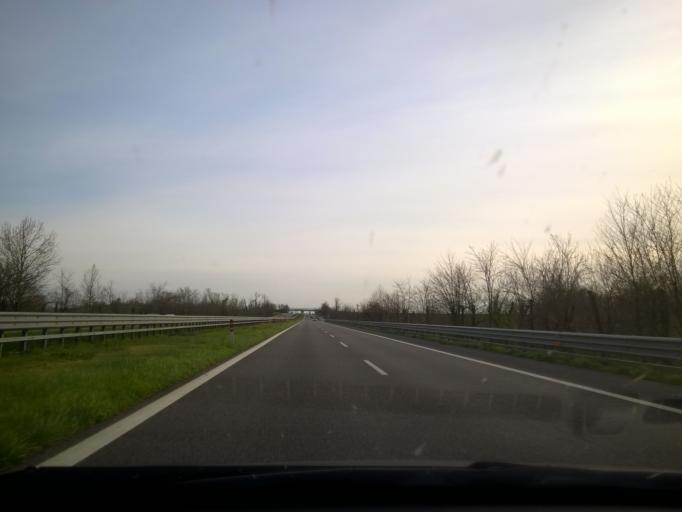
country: IT
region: Lombardy
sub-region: Provincia di Cremona
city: Corte de' Frati
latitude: 45.2437
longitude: 10.1201
